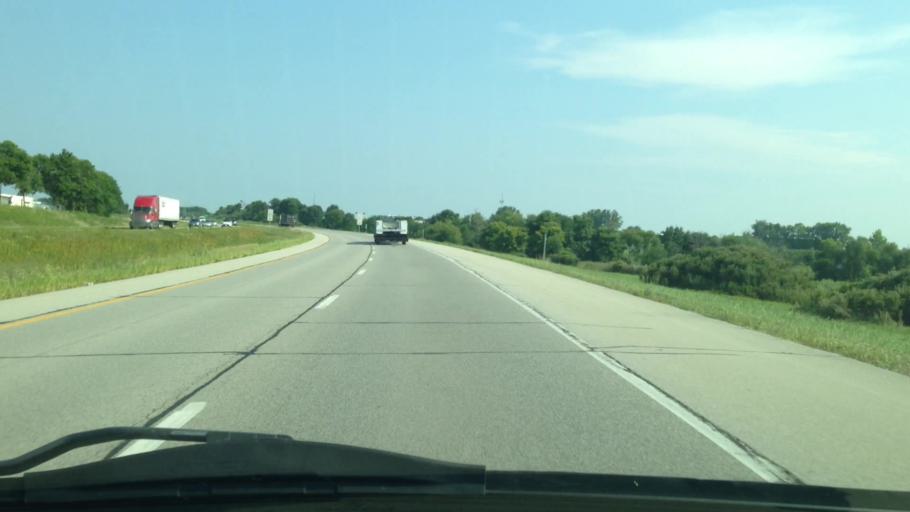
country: US
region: Iowa
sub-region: Linn County
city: Hiawatha
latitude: 42.0532
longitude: -91.6977
